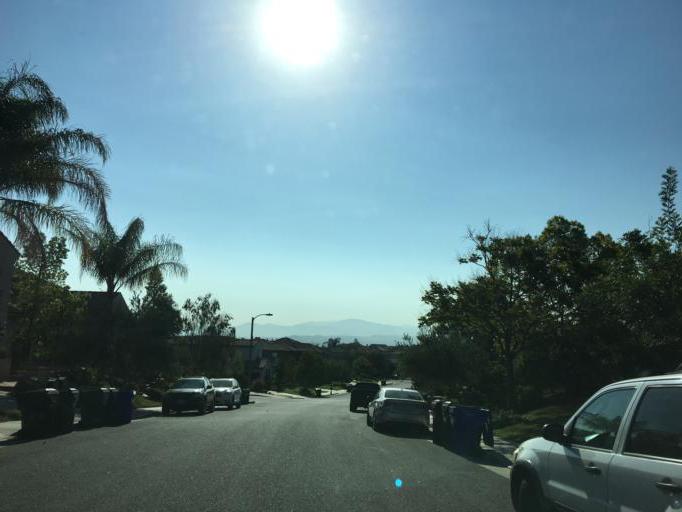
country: US
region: California
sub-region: Los Angeles County
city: Valencia
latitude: 34.4077
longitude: -118.5927
